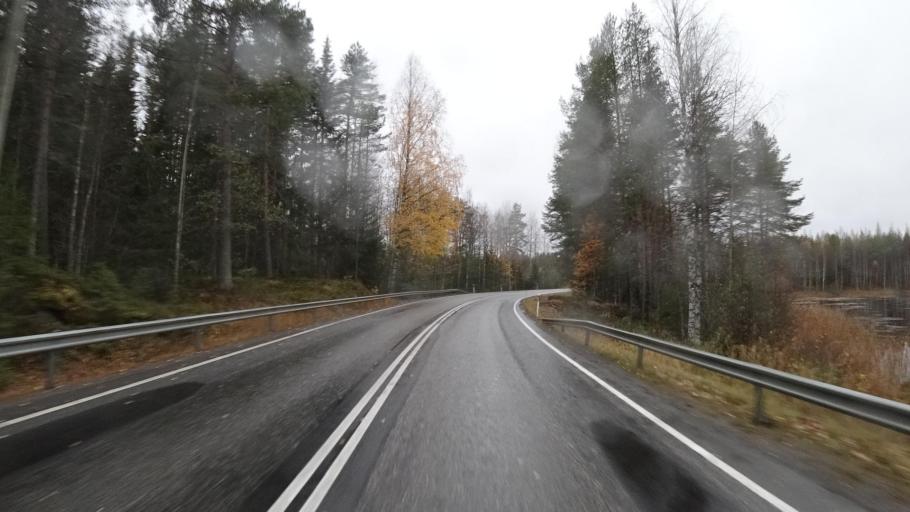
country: FI
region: Northern Savo
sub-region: Koillis-Savo
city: Tuusniemi
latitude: 62.7949
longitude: 28.5283
